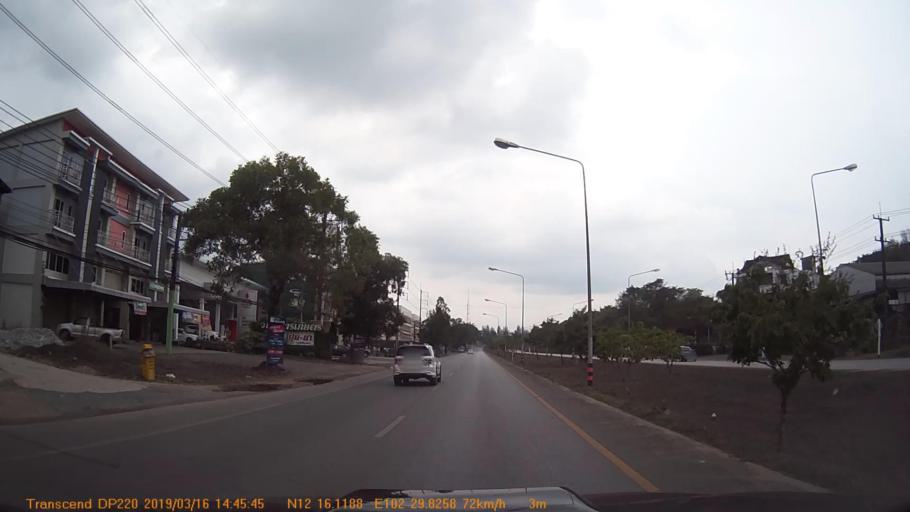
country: TH
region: Trat
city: Trat
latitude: 12.2687
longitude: 102.4970
